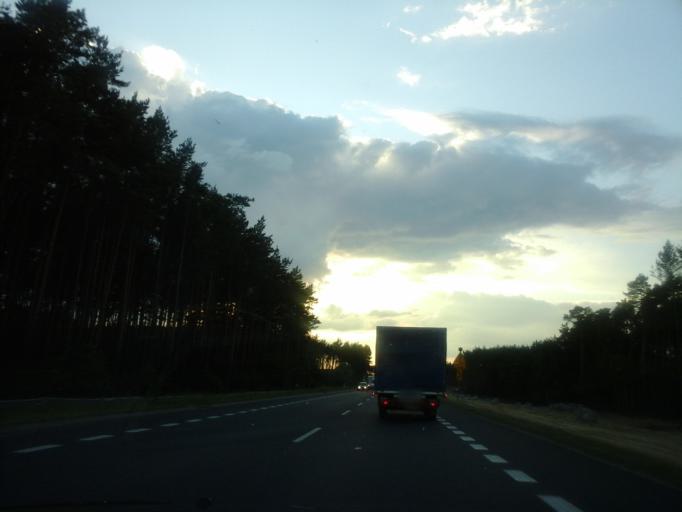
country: PL
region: Lubusz
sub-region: Powiat nowosolski
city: Nowe Miasteczko
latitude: 51.7384
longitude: 15.7164
